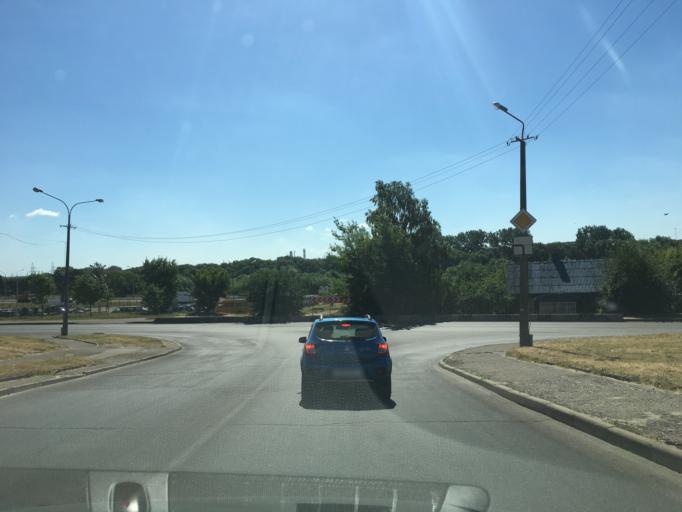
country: BY
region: Grodnenskaya
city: Hrodna
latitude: 53.6941
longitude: 23.8520
